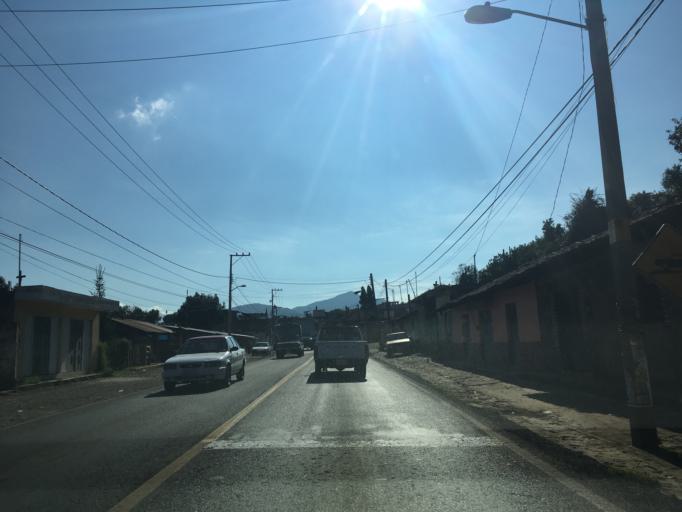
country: MX
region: Mexico
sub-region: Chalco
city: Santo Tomas
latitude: 19.8458
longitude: -102.1012
